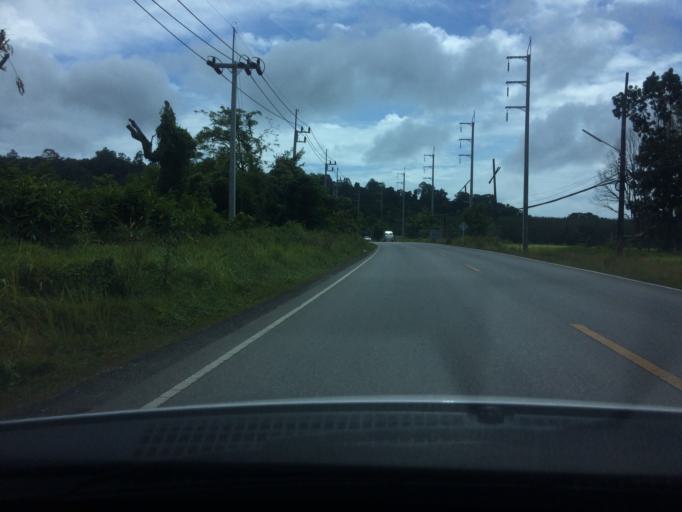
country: TH
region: Phuket
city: Thalang
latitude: 8.0847
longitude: 98.3703
